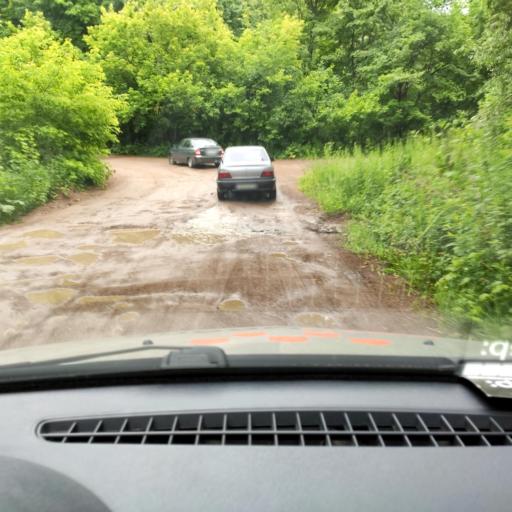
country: RU
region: Bashkortostan
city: Iglino
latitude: 54.8860
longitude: 56.2703
